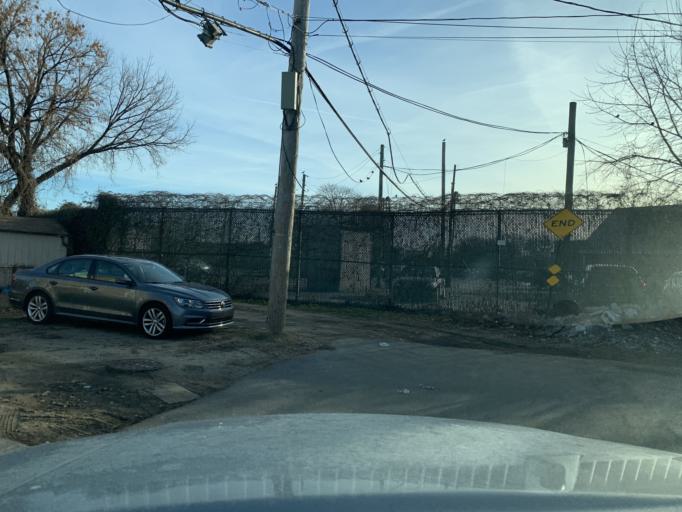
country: US
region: New York
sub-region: Queens County
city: Jamaica
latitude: 40.7012
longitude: -73.7791
